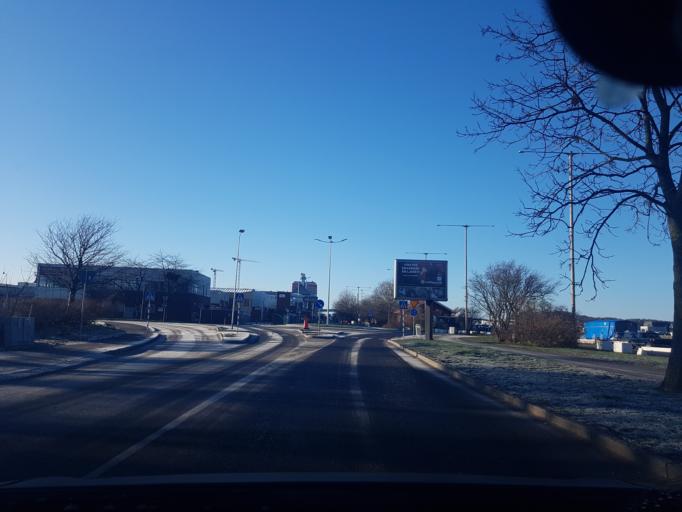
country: SE
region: Vaestra Goetaland
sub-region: Goteborg
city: Goeteborg
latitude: 57.7183
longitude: 11.9810
